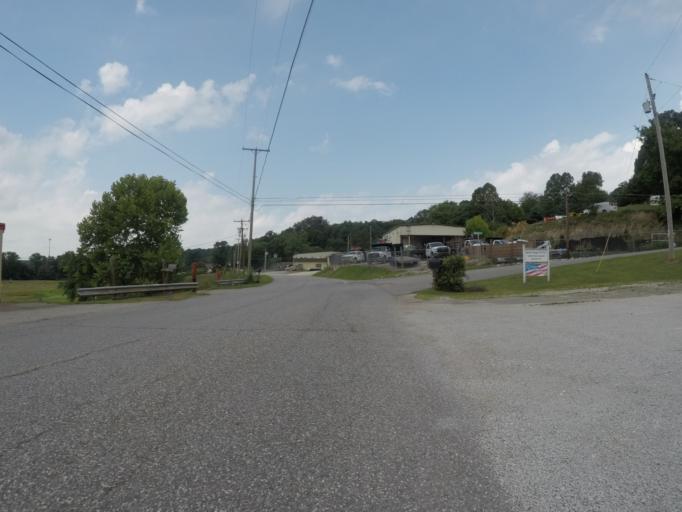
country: US
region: Kentucky
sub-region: Boyd County
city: Meads
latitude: 38.4182
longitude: -82.7071
